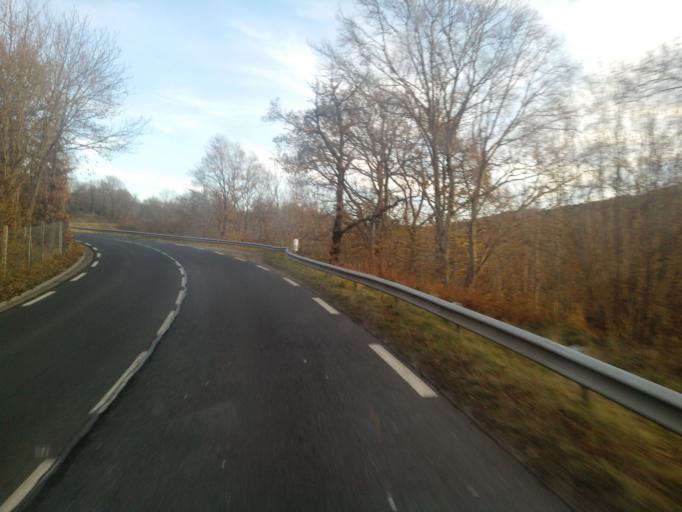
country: FR
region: Auvergne
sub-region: Departement du Cantal
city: Riom-es-Montagnes
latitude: 45.2697
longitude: 2.6661
